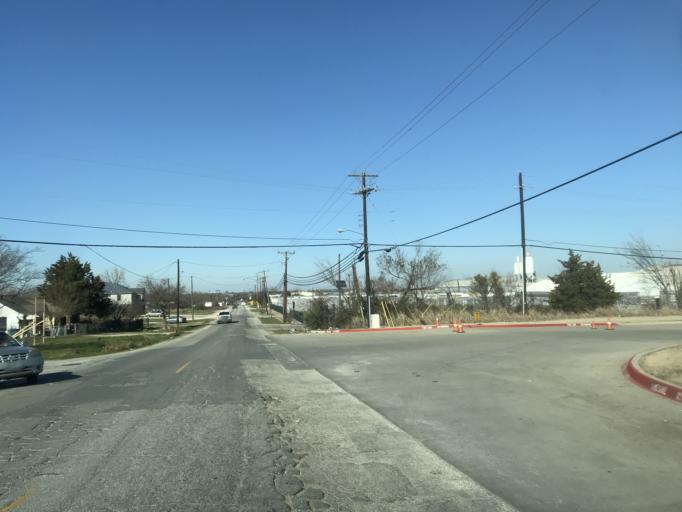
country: US
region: Texas
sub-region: Dallas County
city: Cockrell Hill
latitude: 32.7689
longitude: -96.9027
